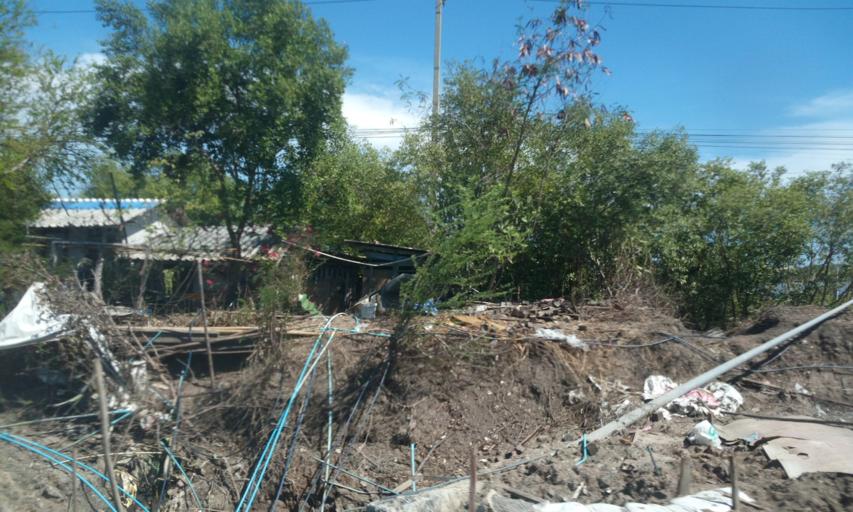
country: TH
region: Samut Prakan
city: Bang Bo District
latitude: 13.5017
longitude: 100.7739
